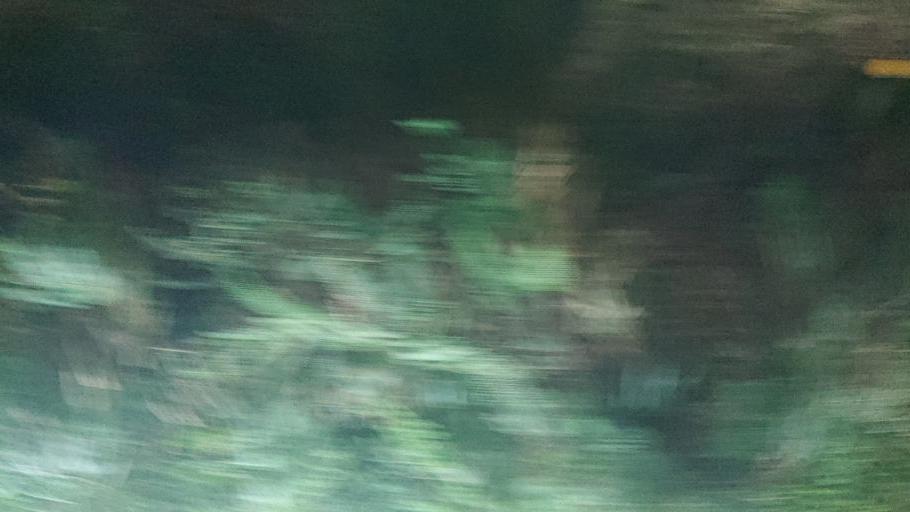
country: TW
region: Taiwan
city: Lugu
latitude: 23.5151
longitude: 120.6990
